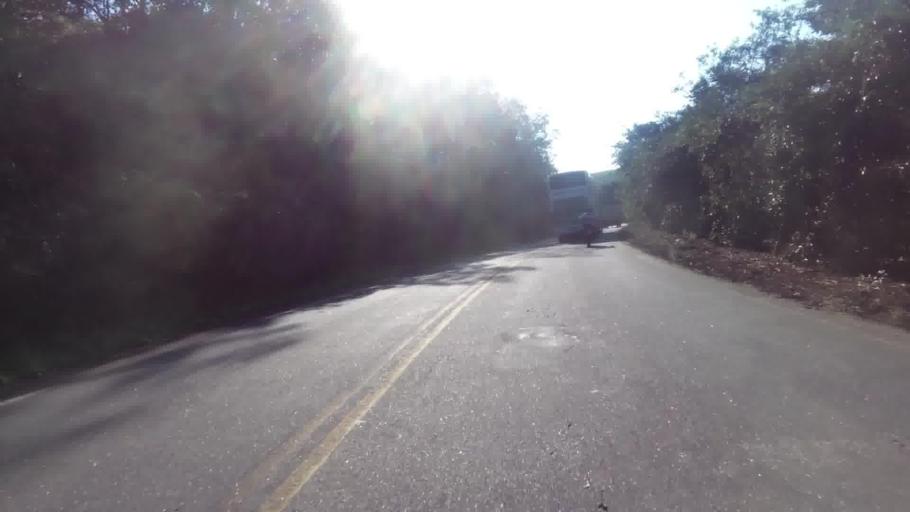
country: BR
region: Espirito Santo
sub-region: Alfredo Chaves
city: Alfredo Chaves
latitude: -20.6738
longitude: -40.7089
